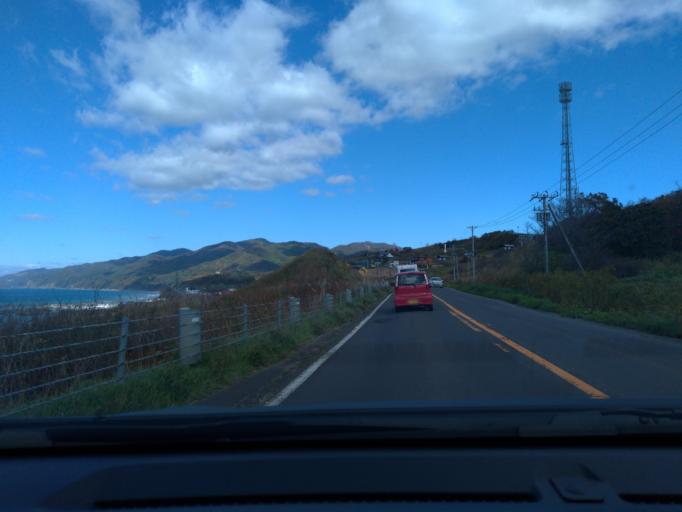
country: JP
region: Hokkaido
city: Ishikari
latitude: 43.3890
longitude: 141.4329
